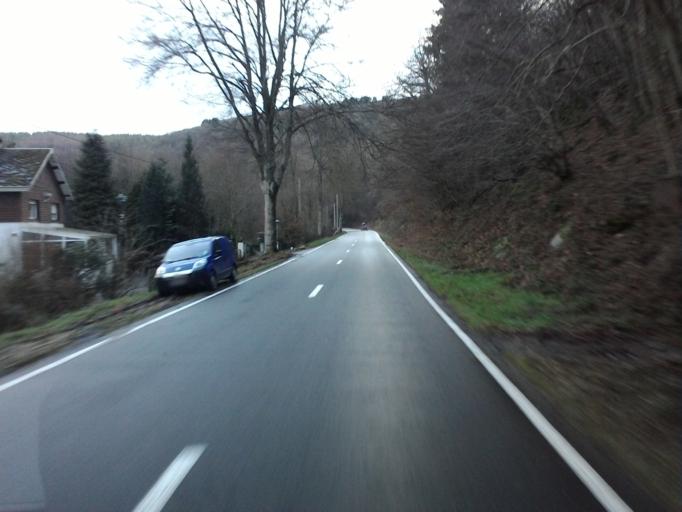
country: BE
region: Wallonia
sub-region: Province de Liege
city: Stoumont
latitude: 50.4013
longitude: 5.7543
